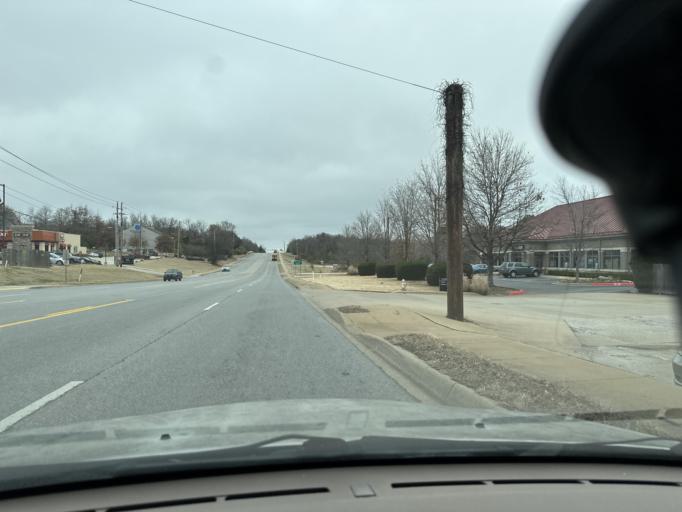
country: US
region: Arkansas
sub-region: Washington County
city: Fayetteville
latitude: 36.0885
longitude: -94.1214
